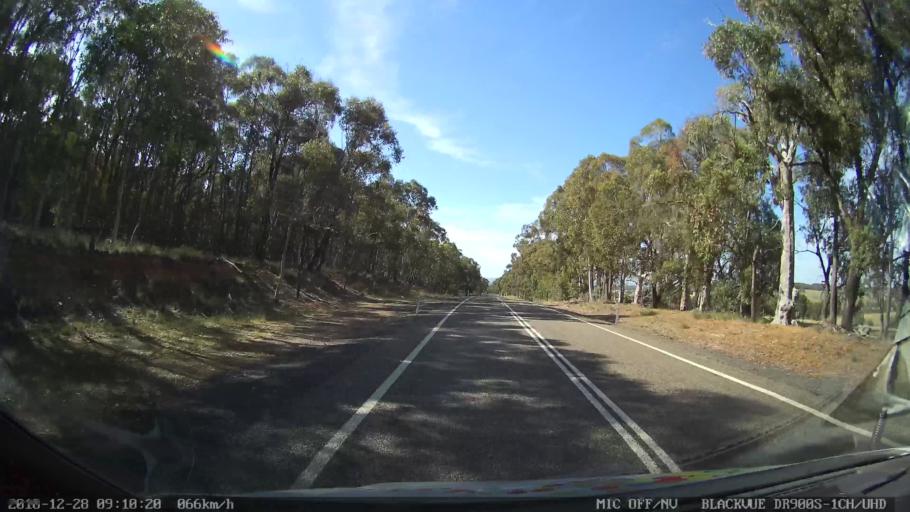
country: AU
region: New South Wales
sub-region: Upper Lachlan Shire
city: Crookwell
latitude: -34.2307
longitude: 149.3363
